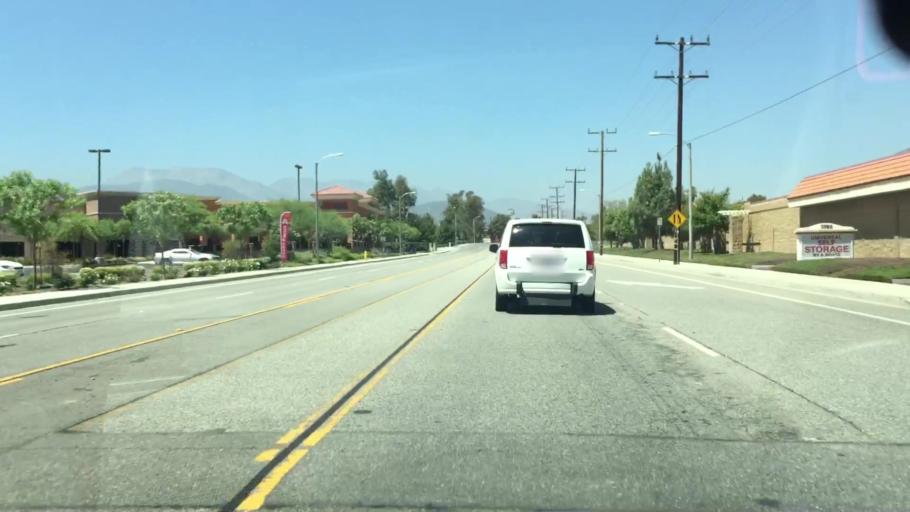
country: US
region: California
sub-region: San Bernardino County
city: Muscoy
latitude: 34.1892
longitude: -117.3561
